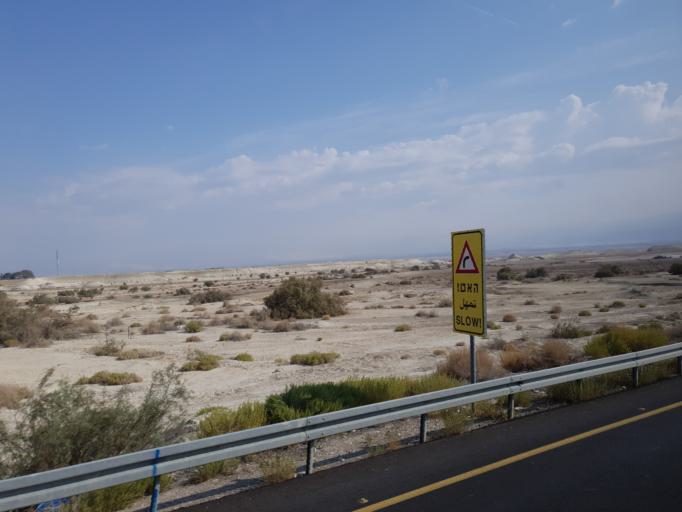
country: PS
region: West Bank
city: Jericho
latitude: 31.7978
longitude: 35.4928
